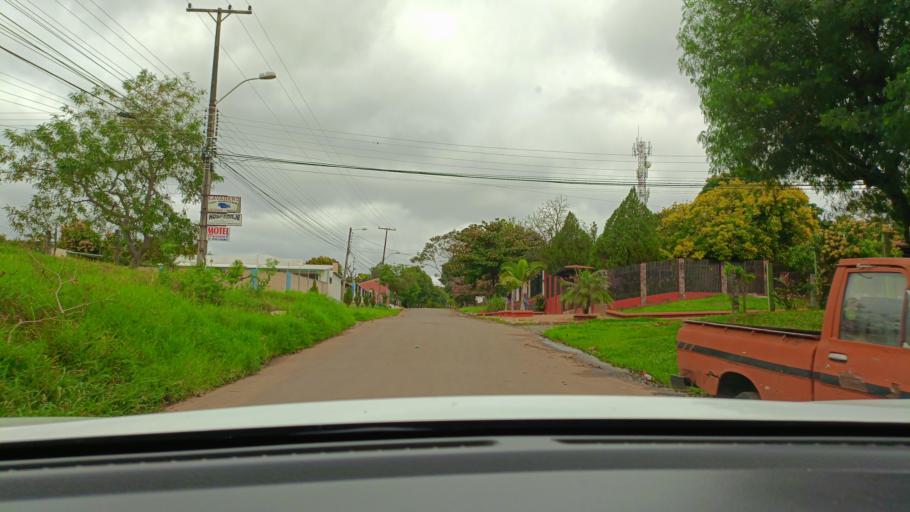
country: PY
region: San Pedro
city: Guayaybi
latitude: -24.6671
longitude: -56.4491
